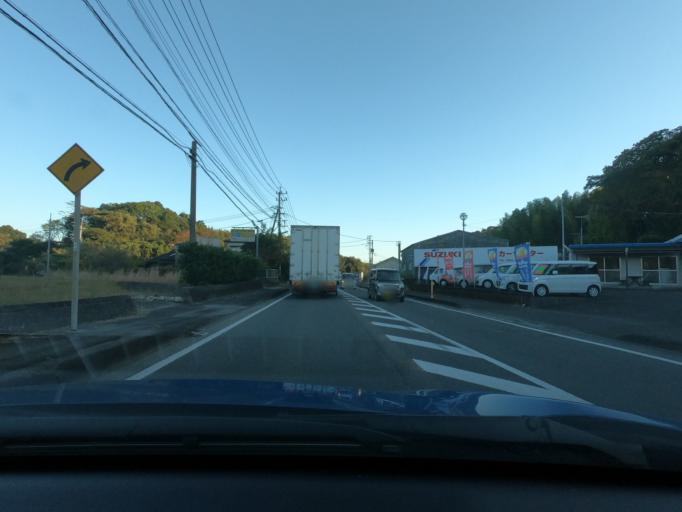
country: JP
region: Kagoshima
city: Satsumasendai
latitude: 31.8417
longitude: 130.2815
